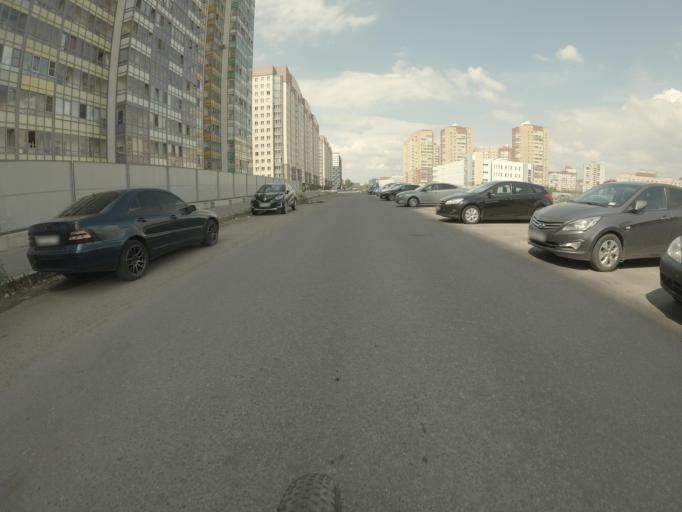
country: RU
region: St.-Petersburg
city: Krasnogvargeisky
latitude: 59.9159
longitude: 30.4410
